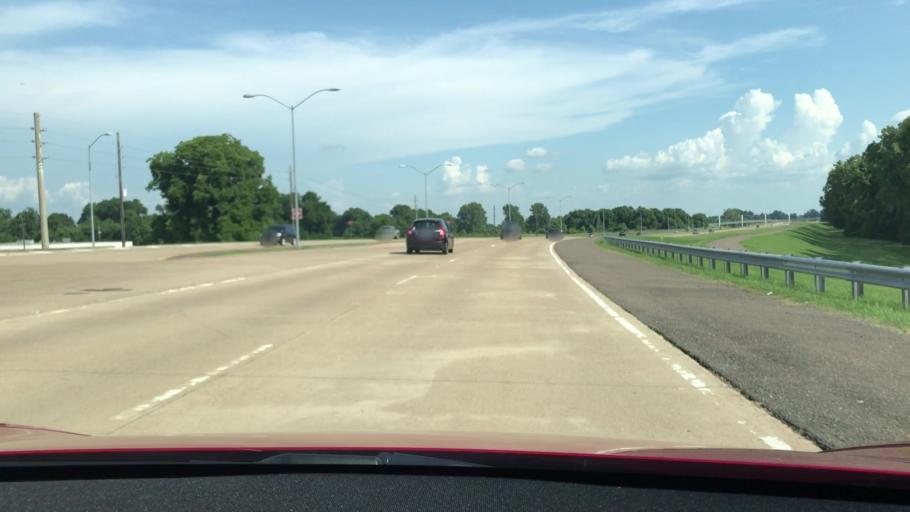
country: US
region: Louisiana
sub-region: Bossier Parish
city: Bossier City
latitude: 32.4784
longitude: -93.6795
